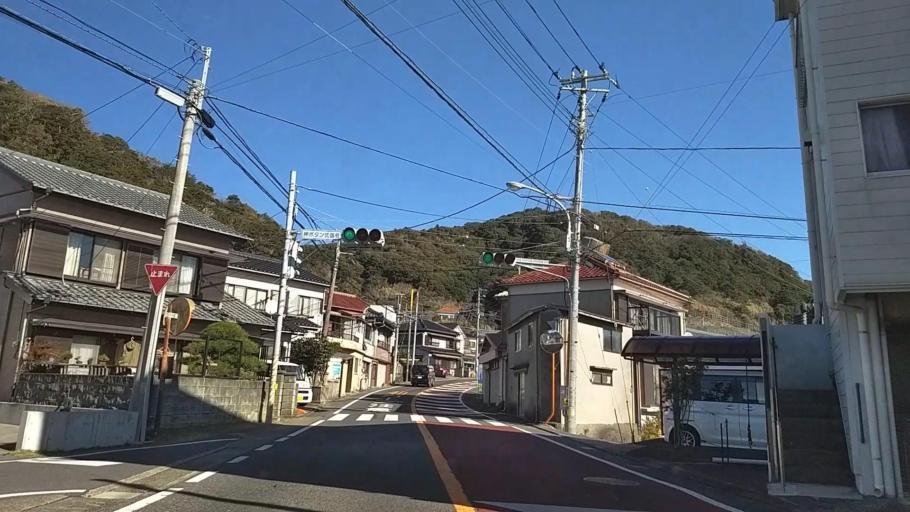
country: JP
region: Chiba
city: Kawaguchi
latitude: 35.0369
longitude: 140.0114
